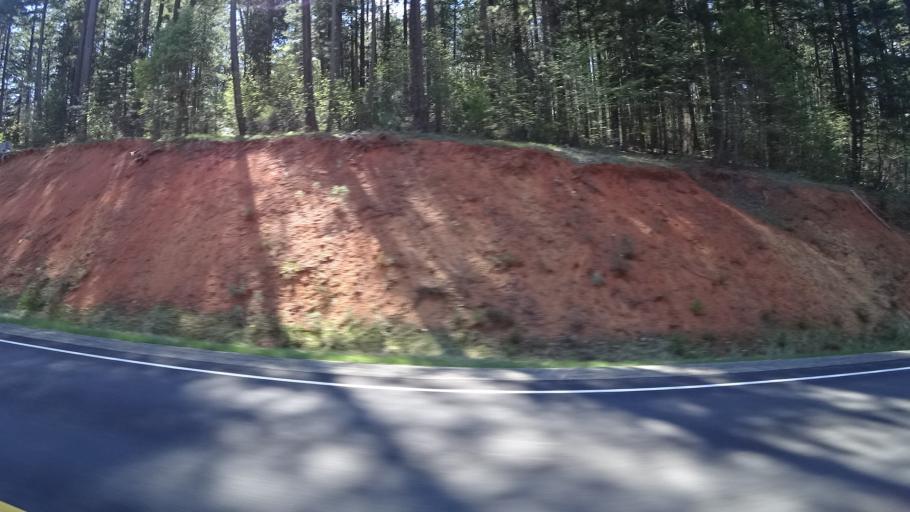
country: US
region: California
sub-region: Trinity County
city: Lewiston
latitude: 40.8848
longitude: -122.7960
